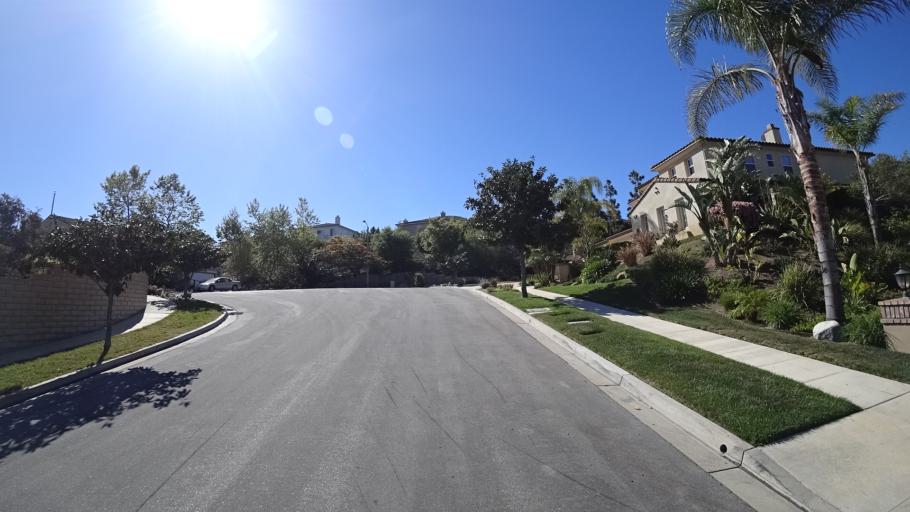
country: US
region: California
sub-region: Ventura County
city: Casa Conejo
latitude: 34.1711
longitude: -118.9844
